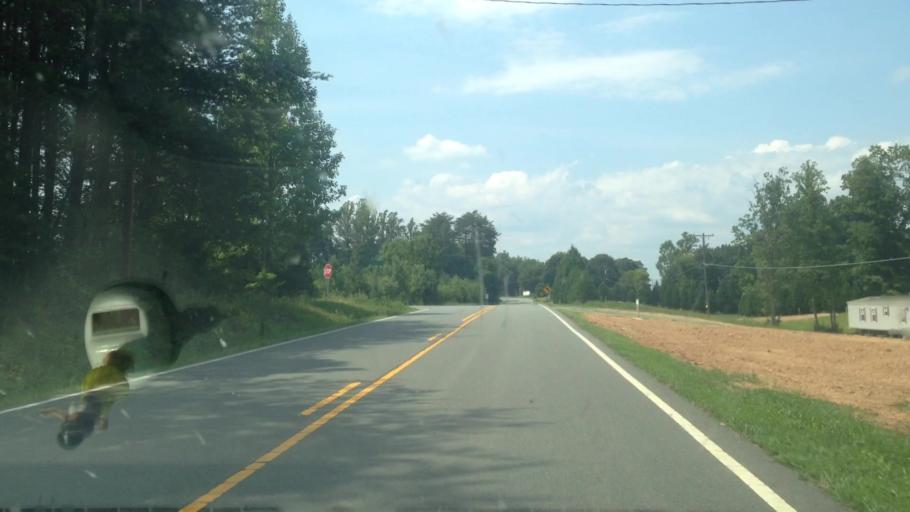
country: US
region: North Carolina
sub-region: Stokes County
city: Walnut Cove
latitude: 36.3675
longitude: -80.0675
